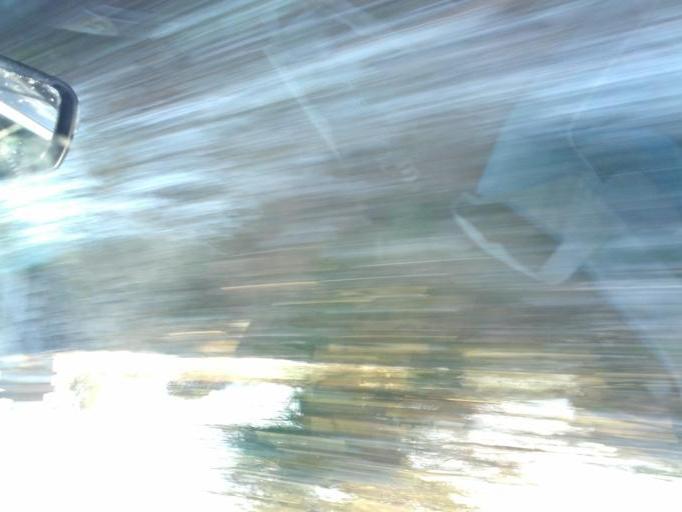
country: IE
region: Connaught
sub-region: County Galway
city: Gort
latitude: 53.1604
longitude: -8.7822
